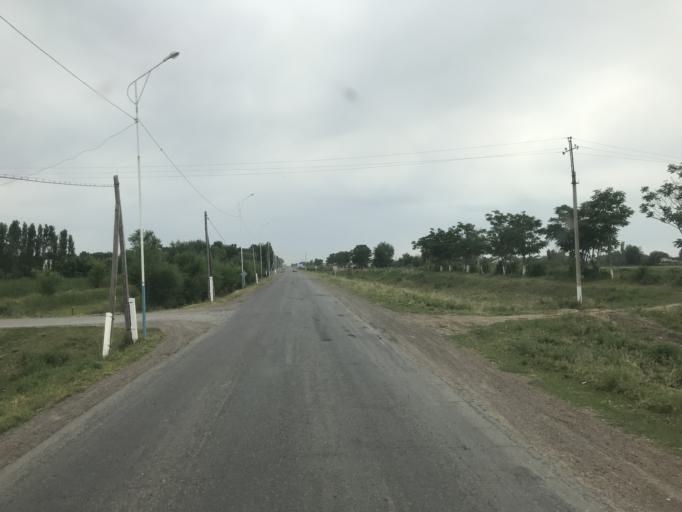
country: KZ
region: Ongtustik Qazaqstan
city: Asykata
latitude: 40.9397
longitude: 68.4135
